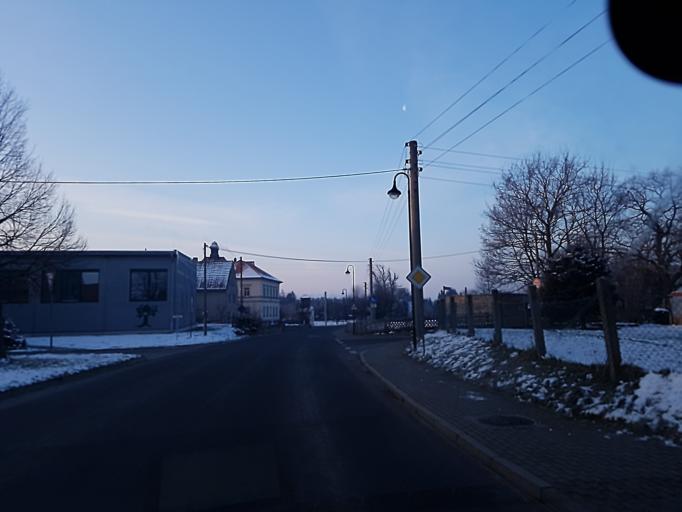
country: DE
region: Saxony
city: Naundorf
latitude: 51.2434
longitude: 13.0815
